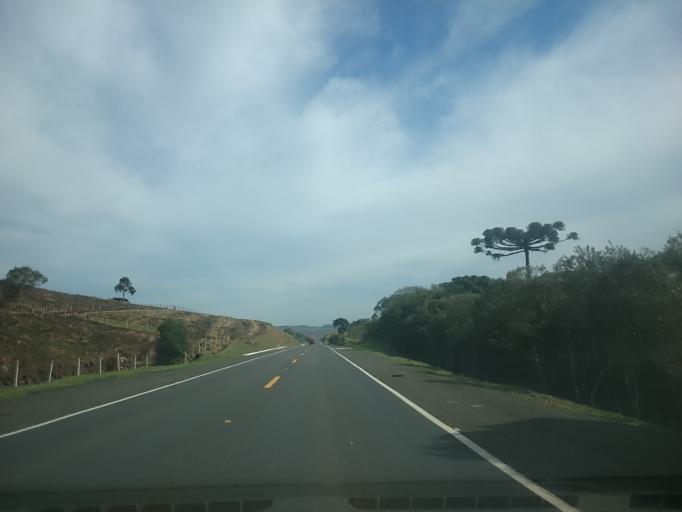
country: BR
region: Rio Grande do Sul
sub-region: Vacaria
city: Estrela
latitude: -28.0813
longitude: -50.5863
